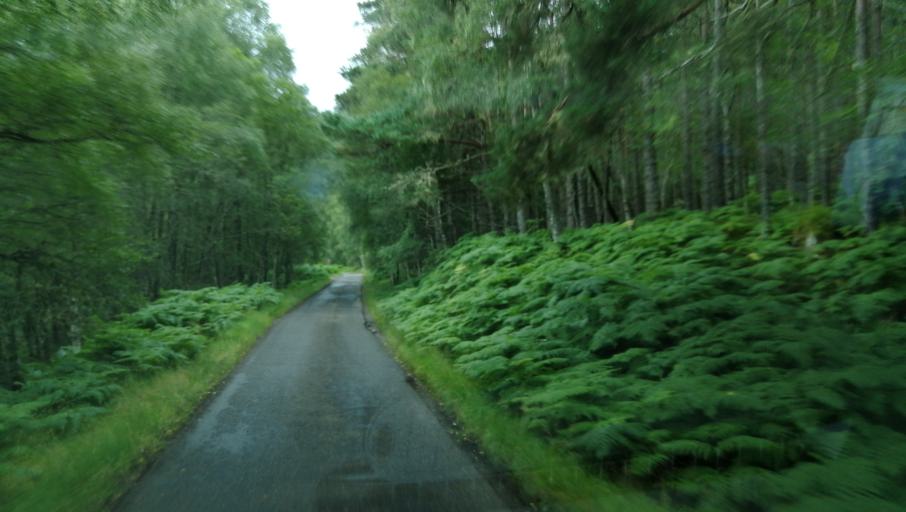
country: GB
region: Scotland
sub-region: Highland
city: Spean Bridge
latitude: 57.3059
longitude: -4.8722
